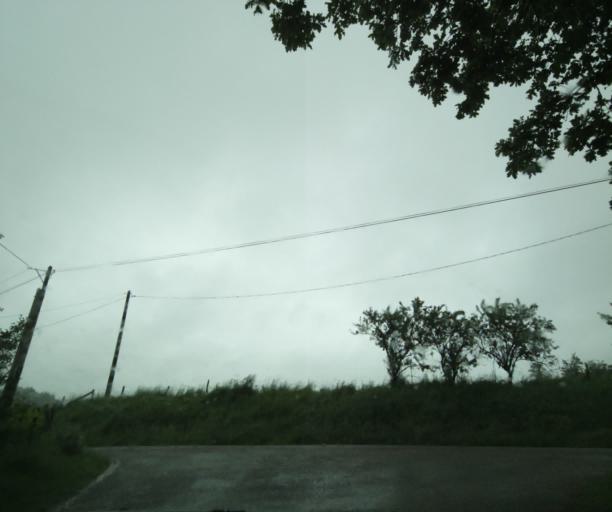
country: FR
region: Bourgogne
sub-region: Departement de Saone-et-Loire
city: Matour
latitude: 46.3698
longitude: 4.3920
